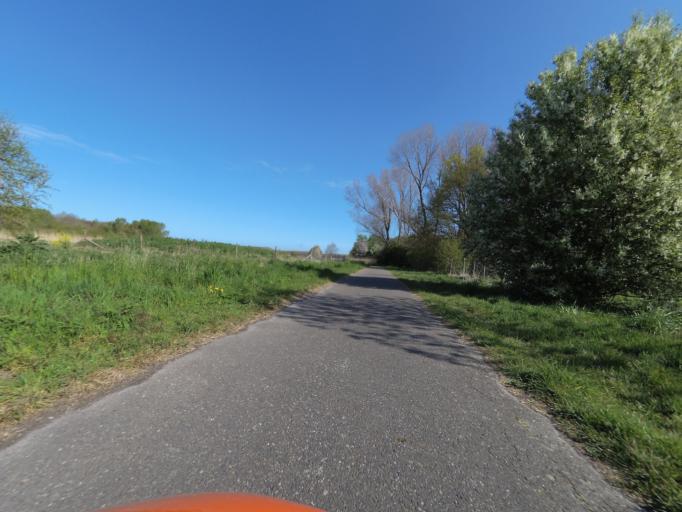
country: NL
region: Flevoland
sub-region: Gemeente Almere
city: Almere Stad
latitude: 52.3685
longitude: 5.1639
